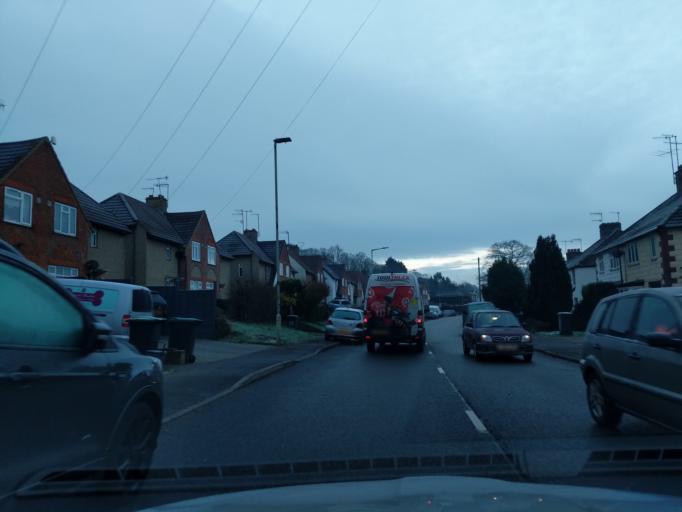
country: GB
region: England
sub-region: Hertfordshire
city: Kings Langley
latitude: 51.7178
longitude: -0.4437
